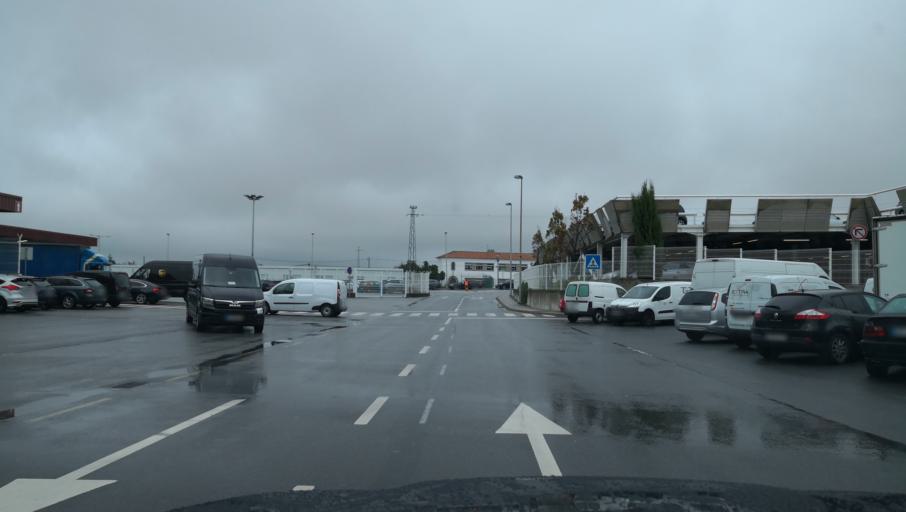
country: PT
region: Porto
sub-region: Matosinhos
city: Santa Cruz do Bispo
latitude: 41.2412
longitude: -8.6714
